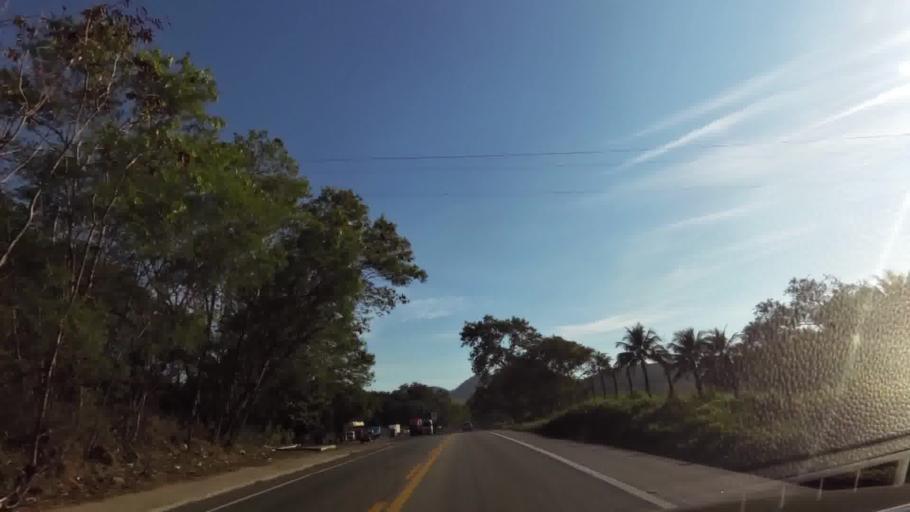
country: BR
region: Espirito Santo
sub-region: Viana
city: Viana
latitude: -20.4120
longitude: -40.4592
